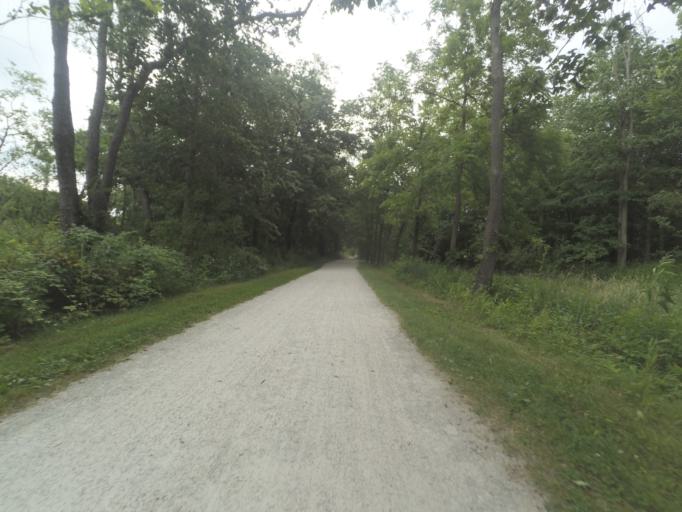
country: US
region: Ohio
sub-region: Summit County
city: Peninsula
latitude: 41.2699
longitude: -81.5595
